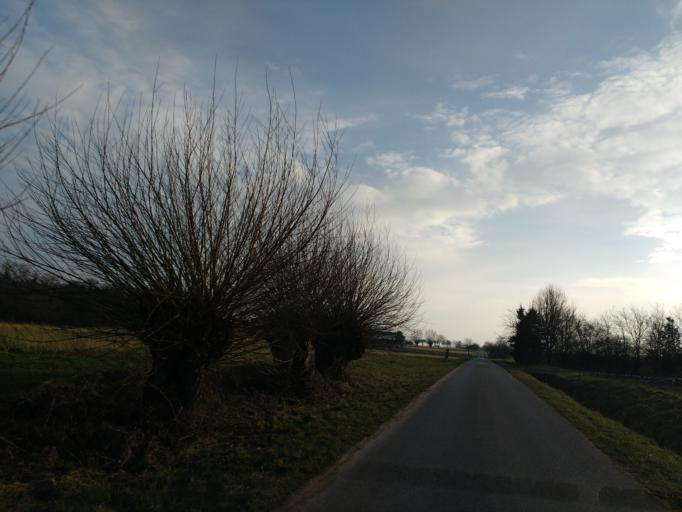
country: DE
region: North Rhine-Westphalia
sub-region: Regierungsbezirk Detmold
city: Paderborn
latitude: 51.7166
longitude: 8.6768
